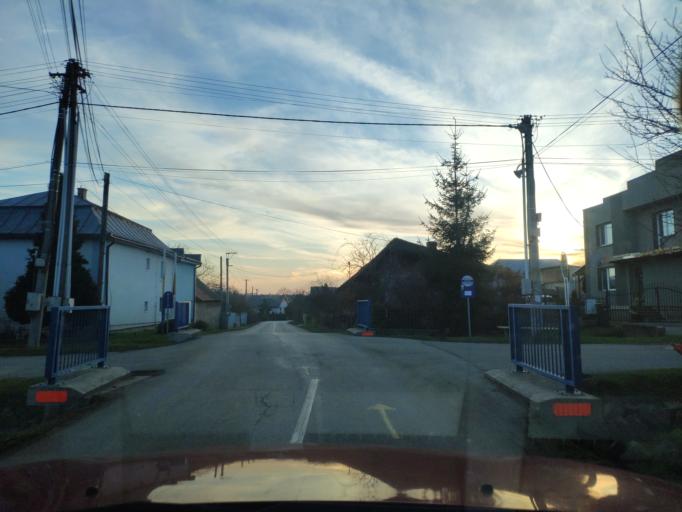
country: SK
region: Kosicky
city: Kosice
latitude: 48.6660
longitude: 21.3981
